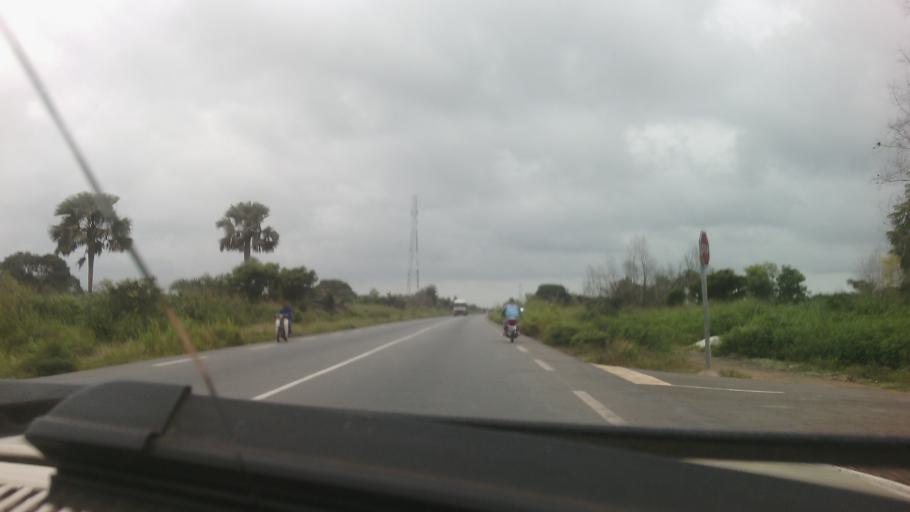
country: BJ
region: Atlantique
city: Ouidah
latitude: 6.3943
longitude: 1.9860
